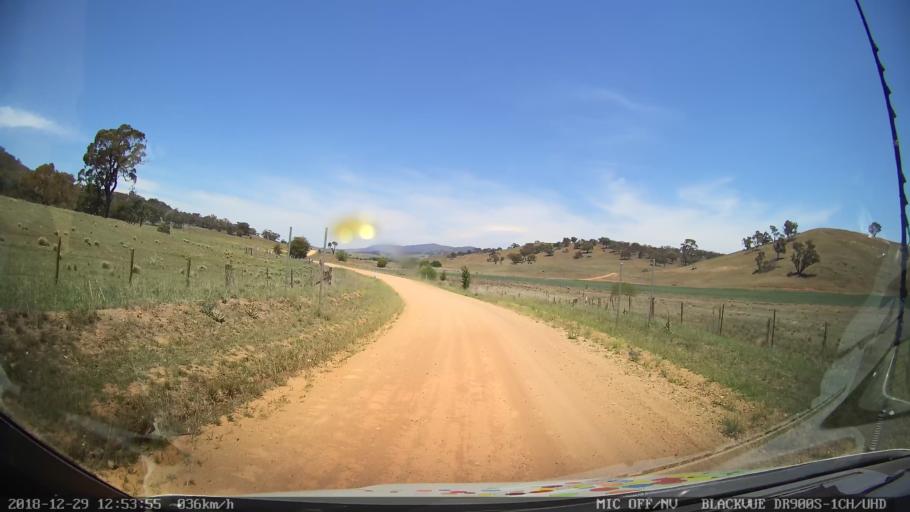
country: AU
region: Australian Capital Territory
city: Macarthur
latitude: -35.6885
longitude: 149.1880
